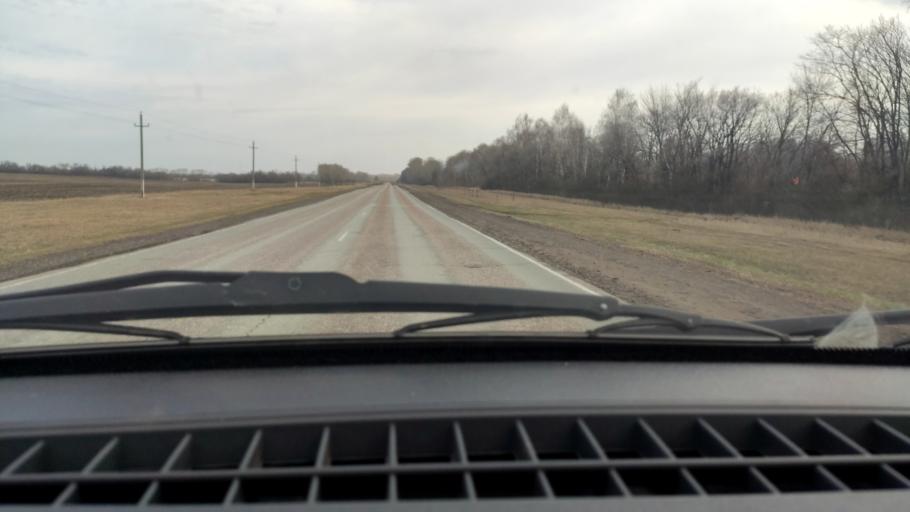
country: RU
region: Bashkortostan
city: Davlekanovo
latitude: 54.3350
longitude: 55.1691
